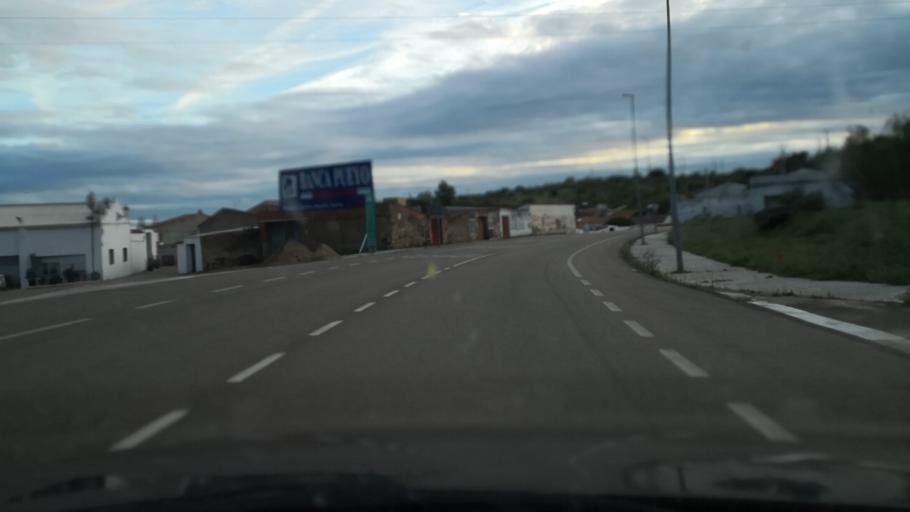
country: ES
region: Extremadura
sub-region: Provincia de Badajoz
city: La Roca de la Sierra
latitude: 39.1130
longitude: -6.6888
